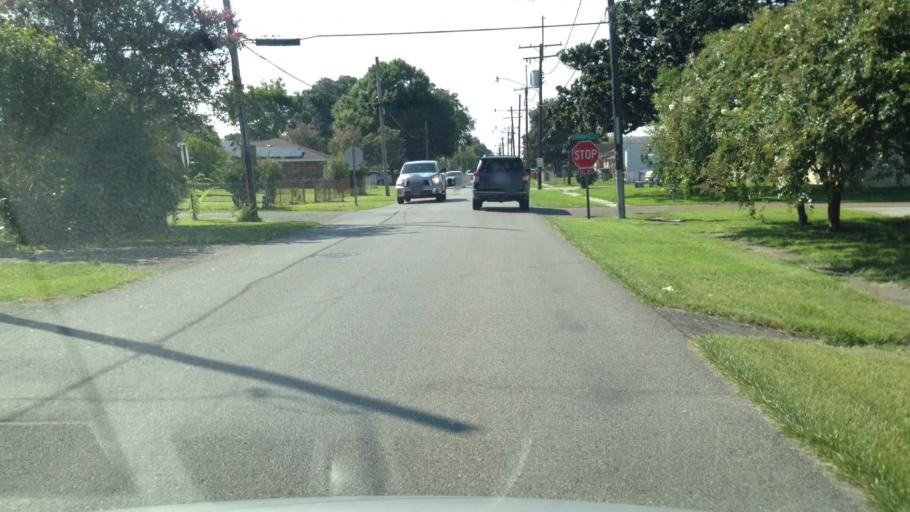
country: US
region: Louisiana
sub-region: Jefferson Parish
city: Bridge City
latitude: 29.9313
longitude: -90.1681
